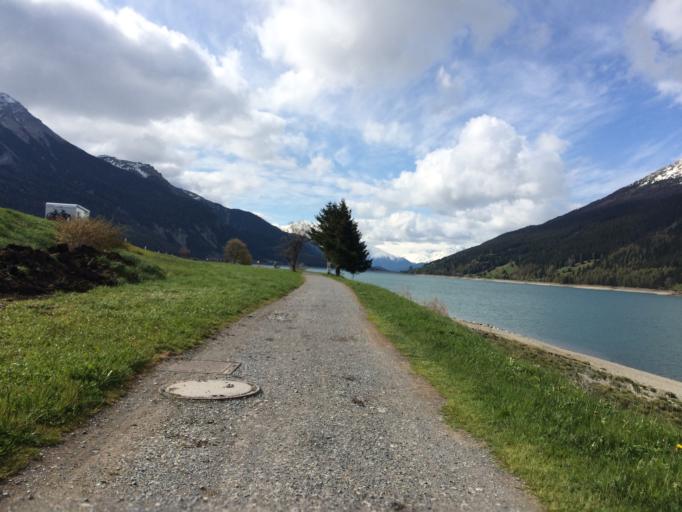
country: IT
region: Trentino-Alto Adige
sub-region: Bolzano
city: Curon Venosta
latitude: 46.8229
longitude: 10.5214
